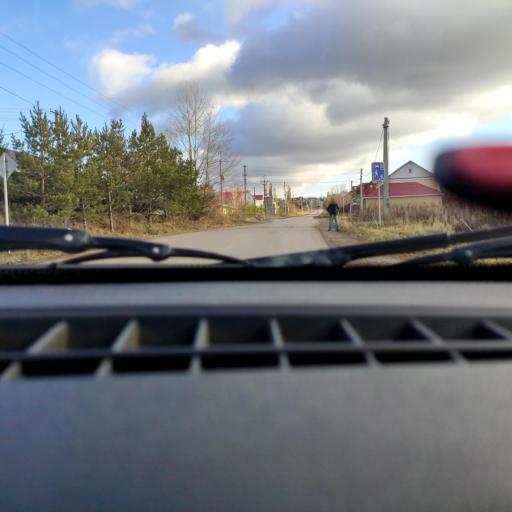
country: RU
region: Bashkortostan
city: Ufa
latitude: 54.5990
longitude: 55.9296
